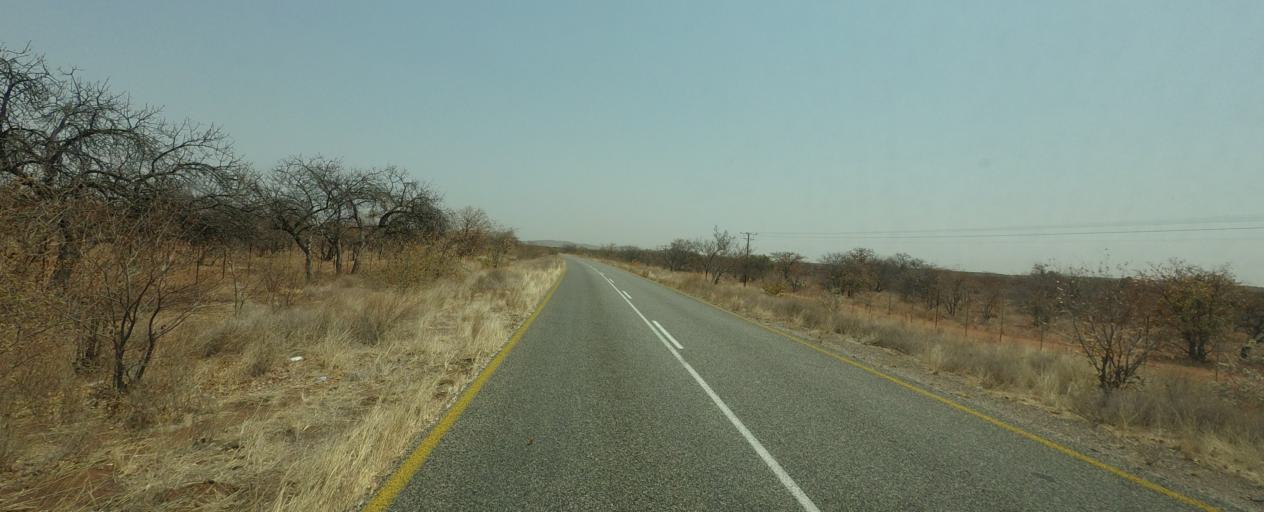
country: ZA
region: Limpopo
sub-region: Vhembe District Municipality
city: Messina
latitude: -22.5911
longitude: 30.2222
